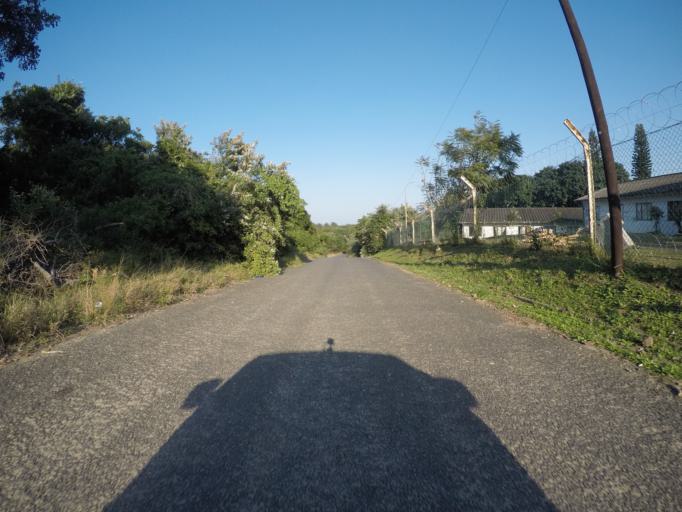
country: ZA
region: KwaZulu-Natal
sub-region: uThungulu District Municipality
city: Richards Bay
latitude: -28.7820
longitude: 32.0872
